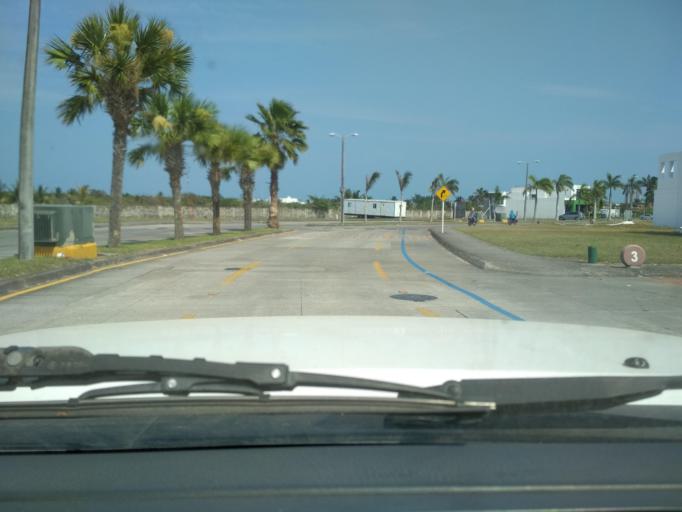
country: MX
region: Veracruz
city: Boca del Rio
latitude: 19.1000
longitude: -96.1175
